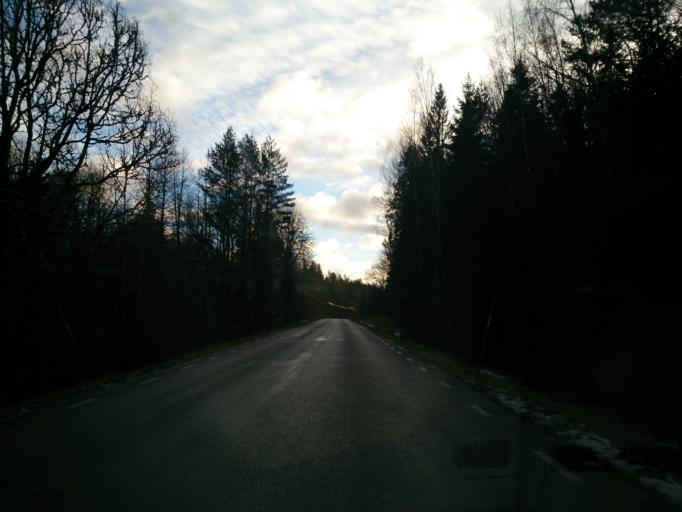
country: SE
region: OEstergoetland
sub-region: Atvidabergs Kommun
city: Atvidaberg
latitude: 58.3211
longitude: 16.0267
